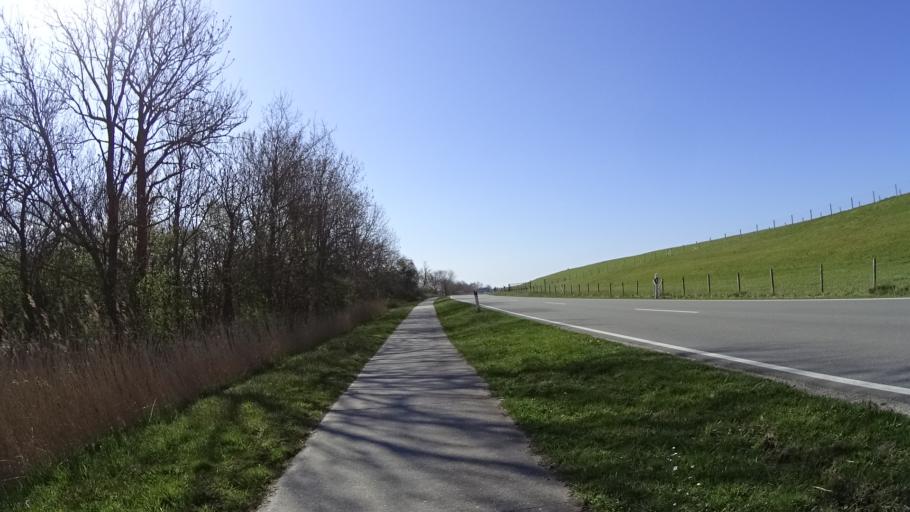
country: DE
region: Lower Saxony
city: Jemgum
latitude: 53.2719
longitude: 7.4077
